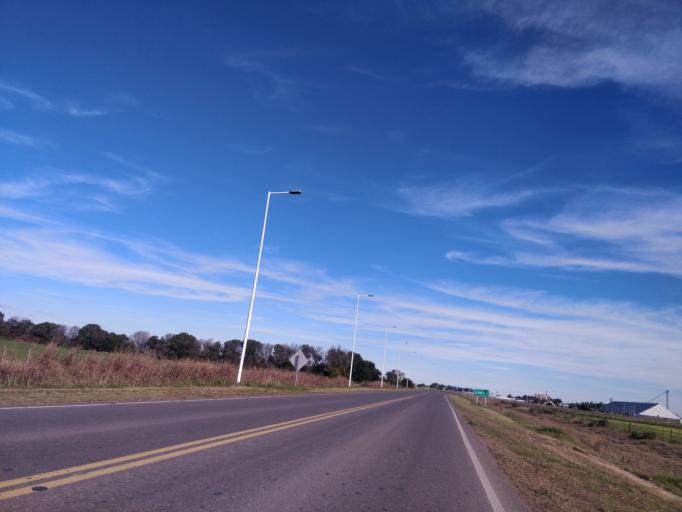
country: AR
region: Cordoba
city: Leones
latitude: -32.6445
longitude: -62.2909
